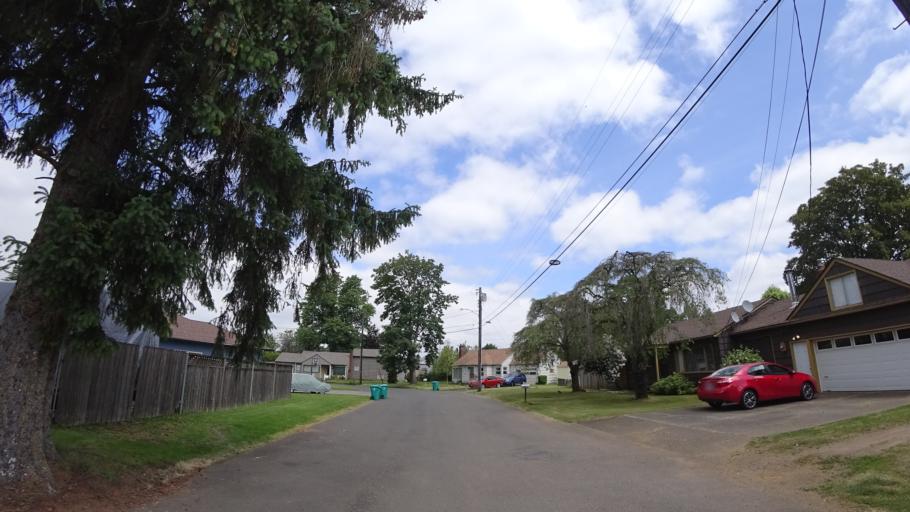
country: US
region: Oregon
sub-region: Multnomah County
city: Gresham
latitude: 45.5032
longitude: -122.4925
